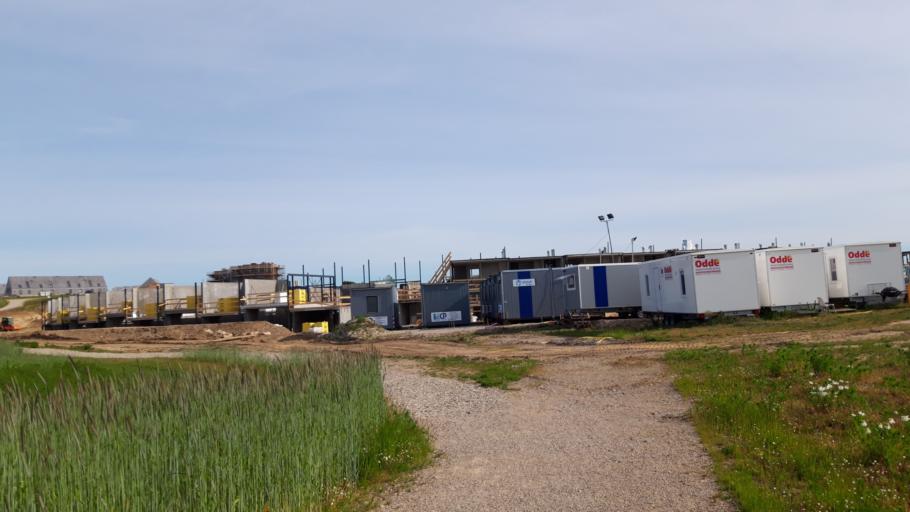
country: DK
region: Central Jutland
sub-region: Arhus Kommune
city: Lystrup
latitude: 56.2317
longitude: 10.2046
